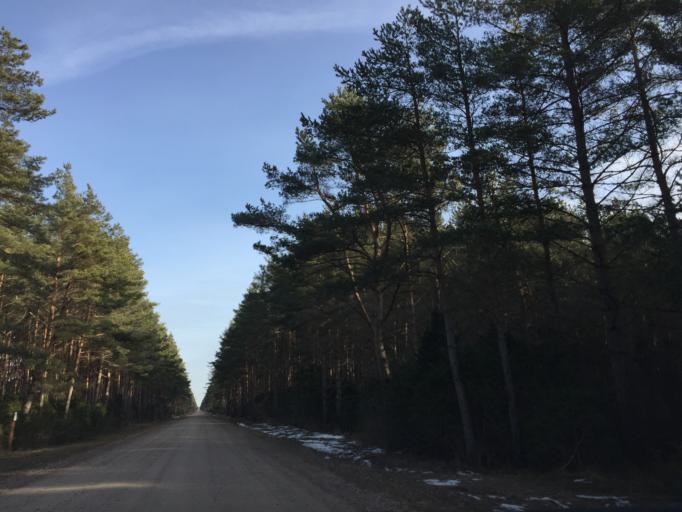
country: EE
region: Saare
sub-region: Kuressaare linn
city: Kuressaare
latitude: 58.2872
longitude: 21.9301
